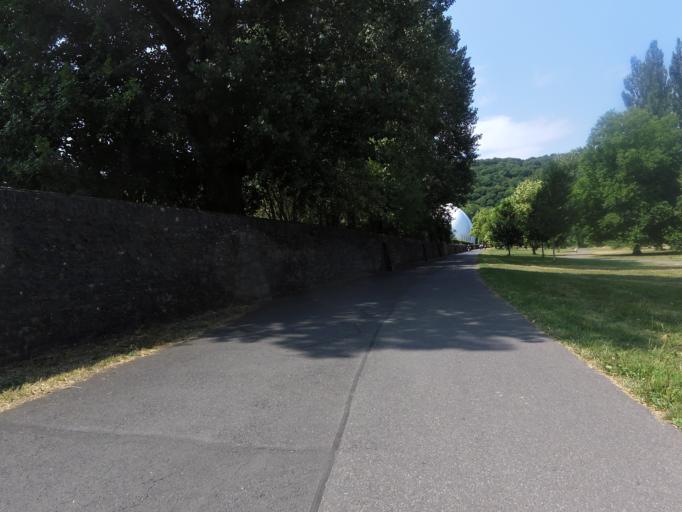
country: DE
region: Bavaria
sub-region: Regierungsbezirk Unterfranken
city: Hochberg
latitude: 49.7971
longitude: 9.8948
